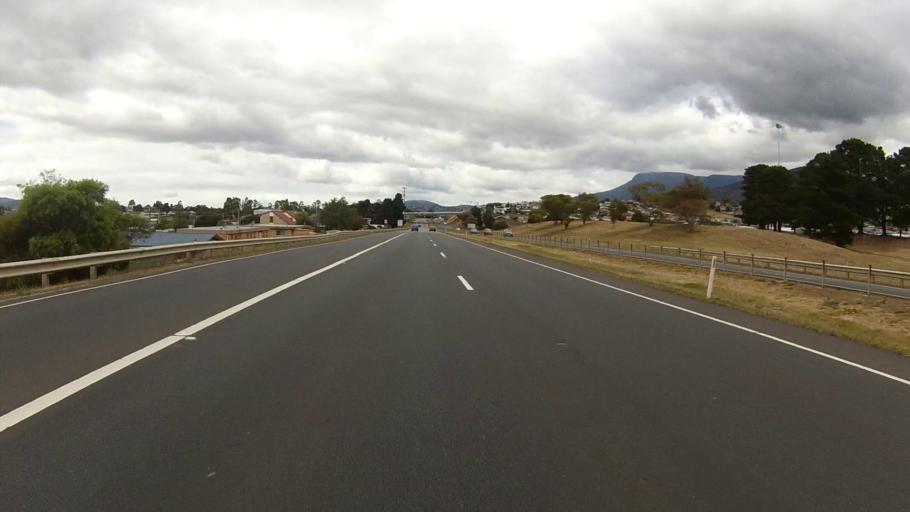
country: AU
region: Tasmania
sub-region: Glenorchy
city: Claremont
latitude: -42.7895
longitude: 147.2452
